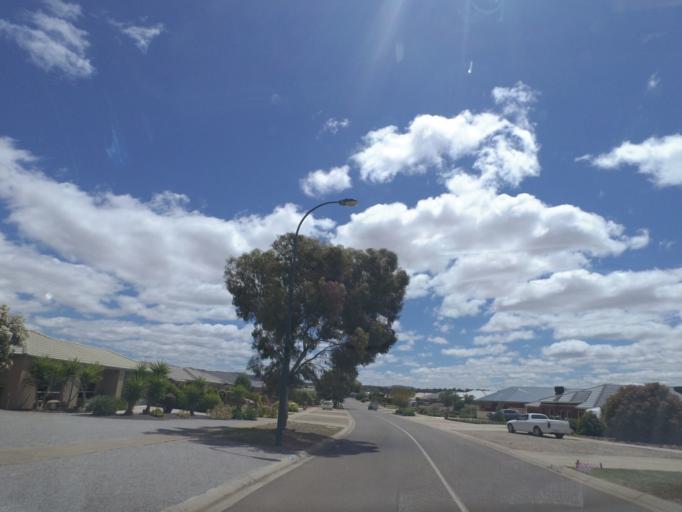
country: AU
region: Victoria
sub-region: Moorabool
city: Bacchus Marsh
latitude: -37.6527
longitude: 144.4380
